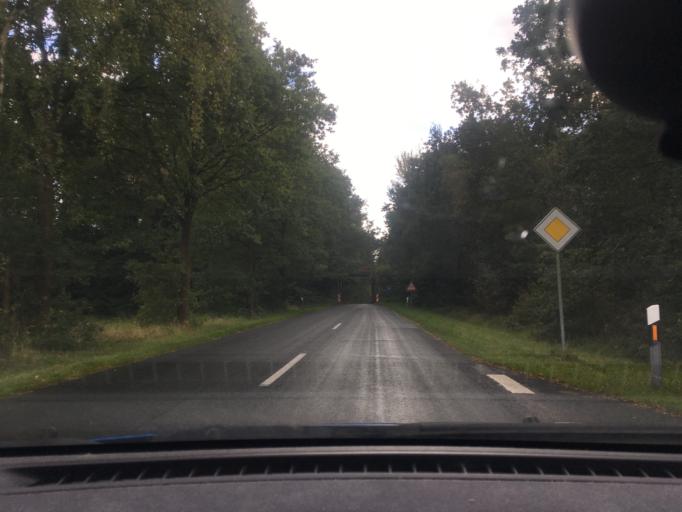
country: DE
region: Lower Saxony
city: Gohrde
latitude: 53.1716
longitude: 10.8726
